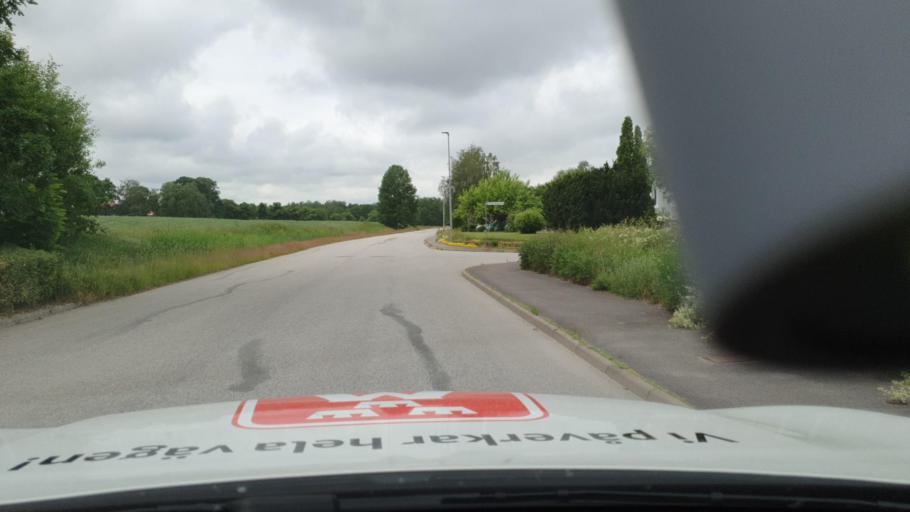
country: SE
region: Vaestra Goetaland
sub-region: Tibro Kommun
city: Tibro
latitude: 58.4037
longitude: 14.1457
